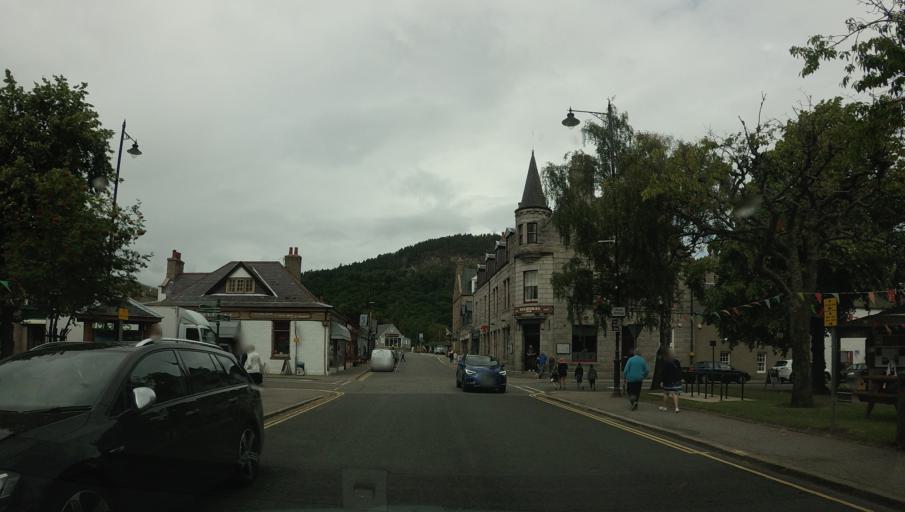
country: GB
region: Scotland
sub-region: Aberdeenshire
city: Ballater
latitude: 57.0492
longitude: -3.0400
